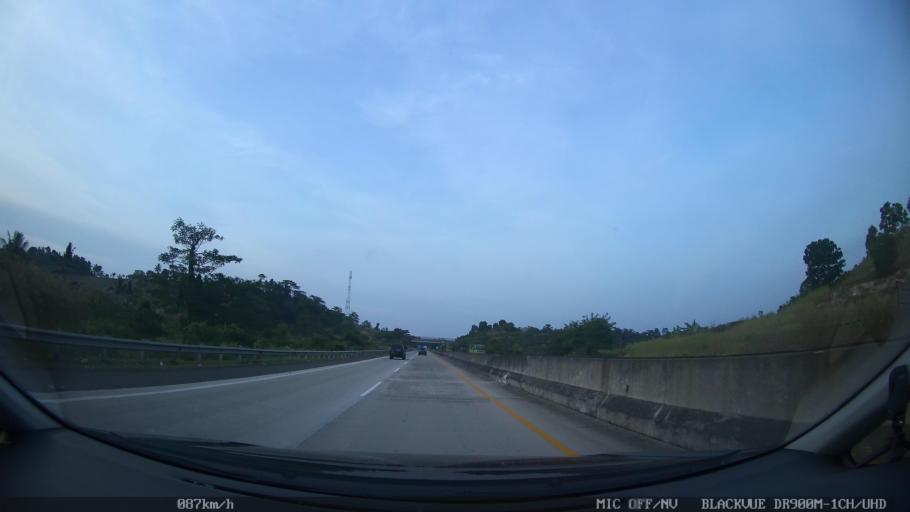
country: ID
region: Lampung
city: Penengahan
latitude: -5.8236
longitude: 105.7352
